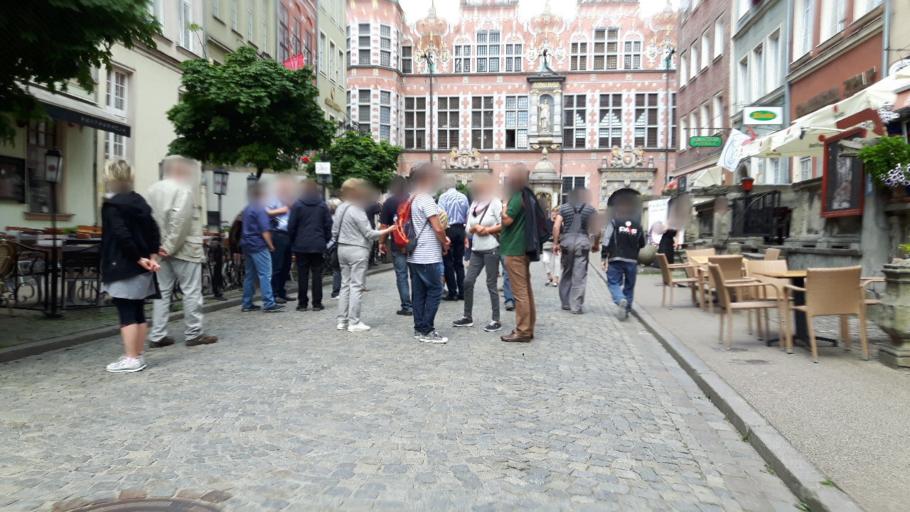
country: PL
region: Pomeranian Voivodeship
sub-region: Gdansk
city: Gdansk
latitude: 54.3504
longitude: 18.6502
